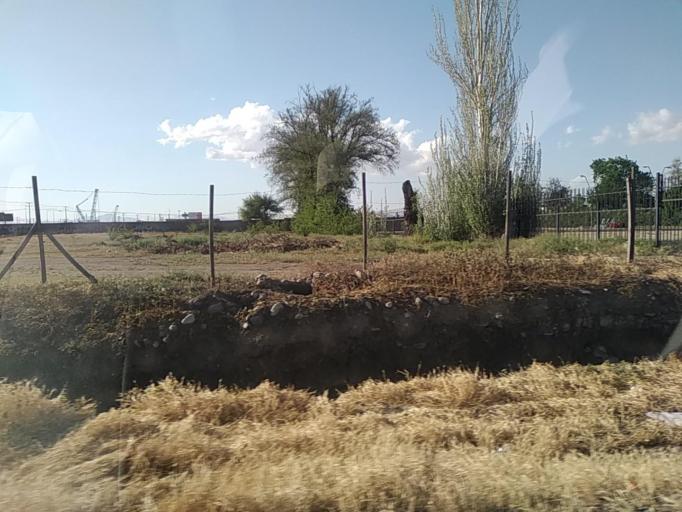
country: CL
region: Santiago Metropolitan
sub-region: Provincia de Chacabuco
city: Chicureo Abajo
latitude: -33.3130
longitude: -70.7226
